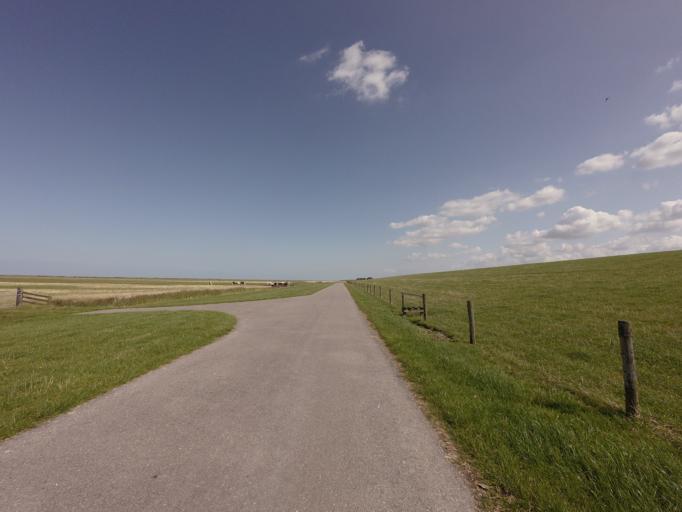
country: NL
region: Friesland
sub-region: Gemeente Ferwerderadiel
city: Marrum
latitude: 53.3422
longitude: 5.7920
